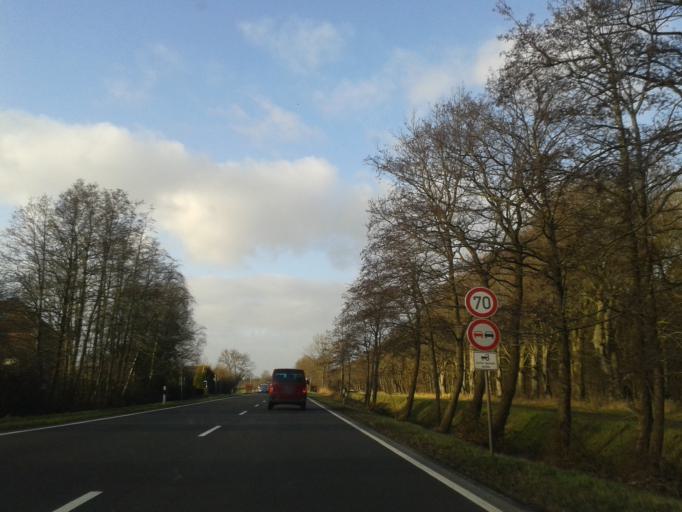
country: DE
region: Lower Saxony
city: Lutetsburg
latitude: 53.5732
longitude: 7.2382
